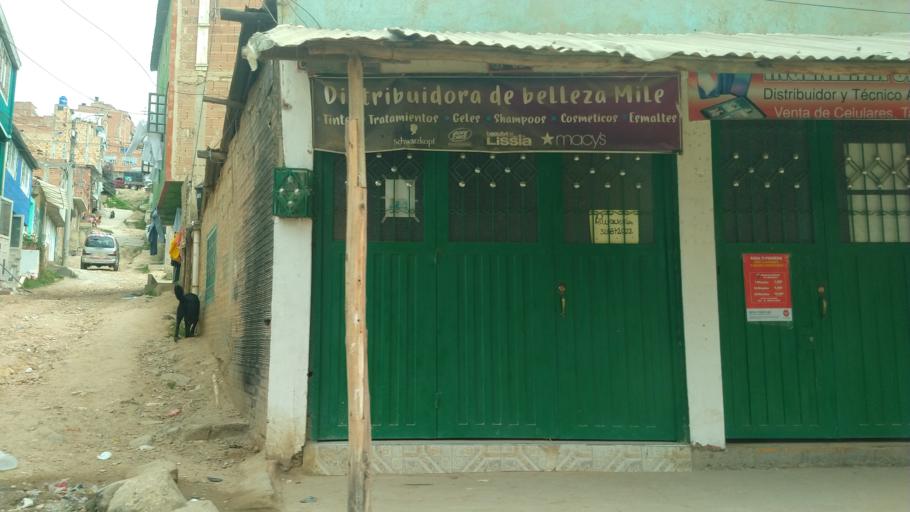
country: CO
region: Cundinamarca
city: Soacha
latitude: 4.5738
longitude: -74.1824
